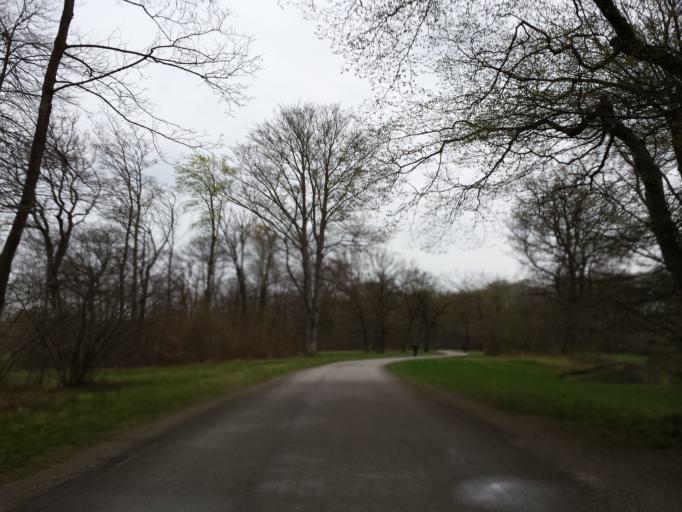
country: DE
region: Bavaria
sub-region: Upper Bavaria
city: Bogenhausen
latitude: 48.1746
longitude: 11.6139
